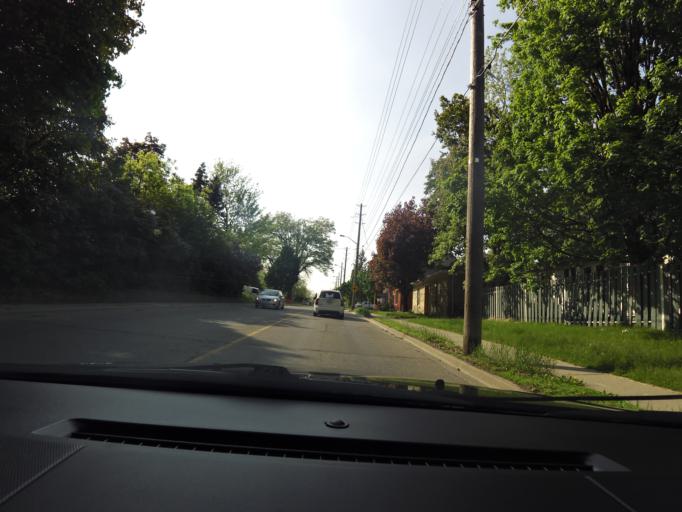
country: CA
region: Ontario
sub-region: Wellington County
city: Guelph
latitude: 43.5365
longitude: -80.2565
